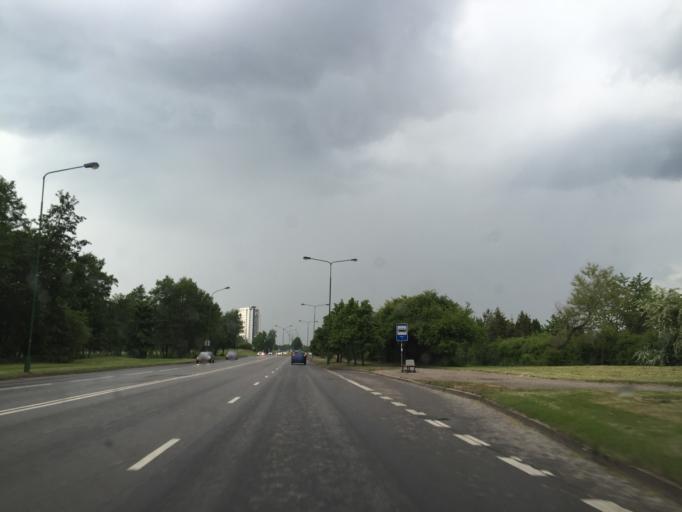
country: LT
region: Klaipedos apskritis
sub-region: Klaipeda
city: Klaipeda
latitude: 55.7417
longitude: 21.1302
